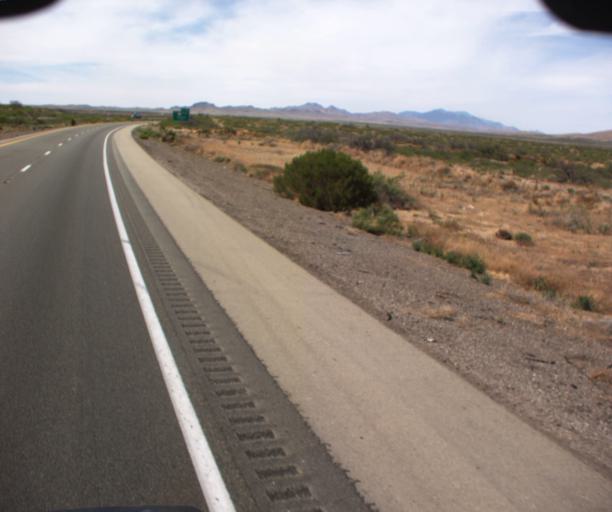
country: US
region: Arizona
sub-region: Cochise County
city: Willcox
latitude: 32.3479
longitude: -109.6015
